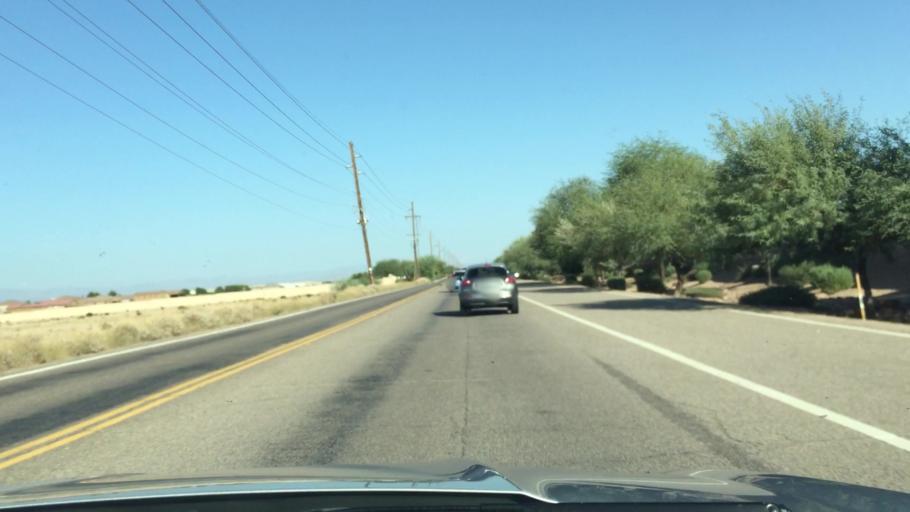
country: US
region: Arizona
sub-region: Maricopa County
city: Queen Creek
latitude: 33.2051
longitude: -111.6282
